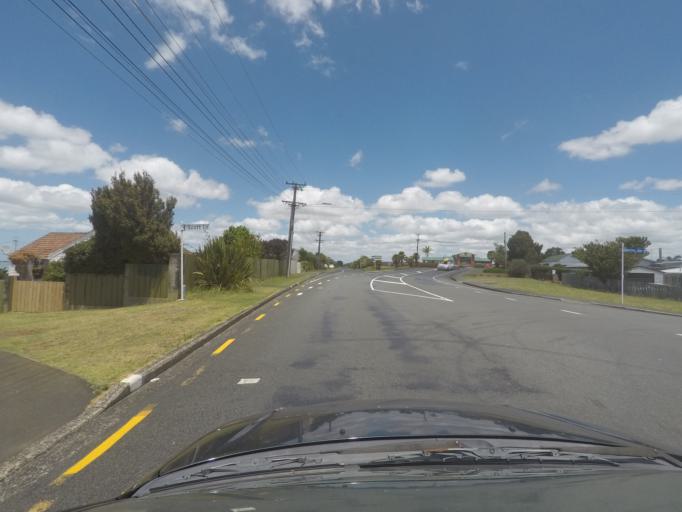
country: NZ
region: Northland
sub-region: Whangarei
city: Whangarei
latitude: -35.7641
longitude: 174.3673
